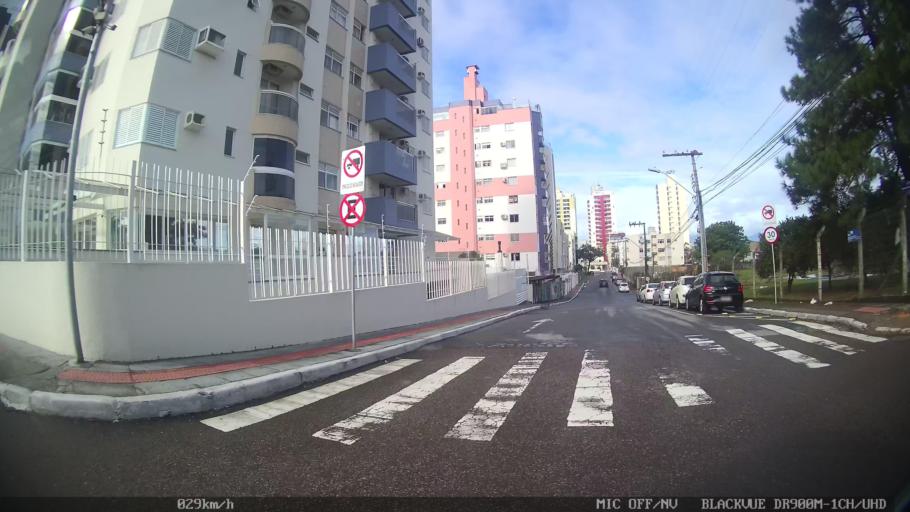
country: BR
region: Santa Catarina
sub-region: Sao Jose
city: Campinas
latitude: -27.5913
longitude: -48.6160
